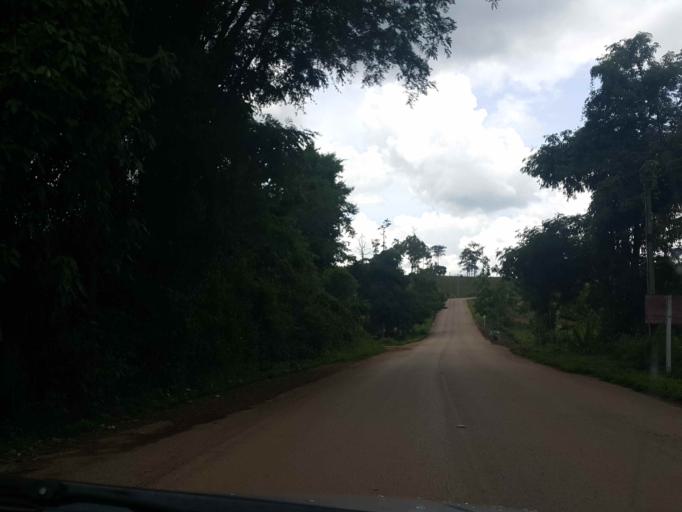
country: TH
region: Lampang
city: Ngao
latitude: 18.9503
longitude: 100.0769
